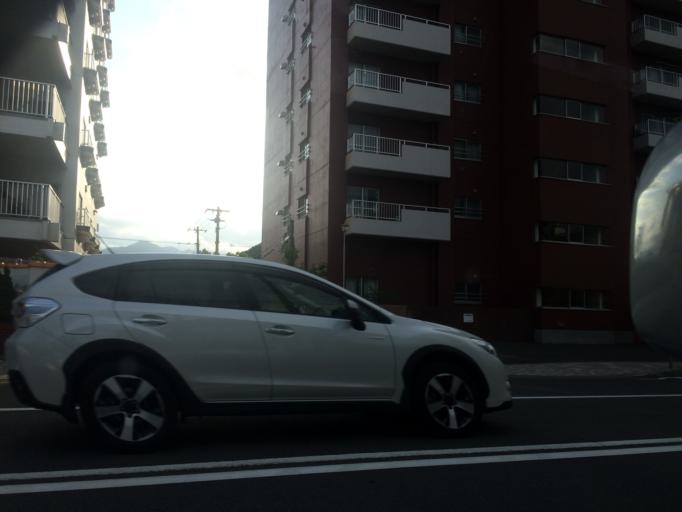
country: JP
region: Hokkaido
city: Sapporo
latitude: 43.0024
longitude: 141.3484
